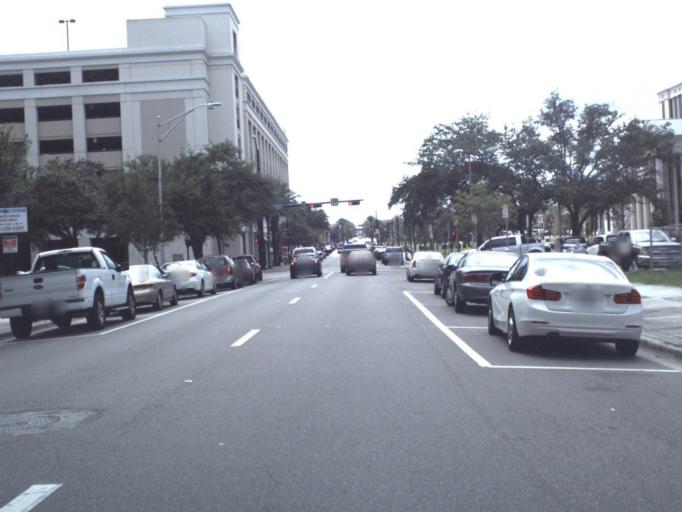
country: US
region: Florida
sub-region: Duval County
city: Jacksonville
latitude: 30.3287
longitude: -81.6617
